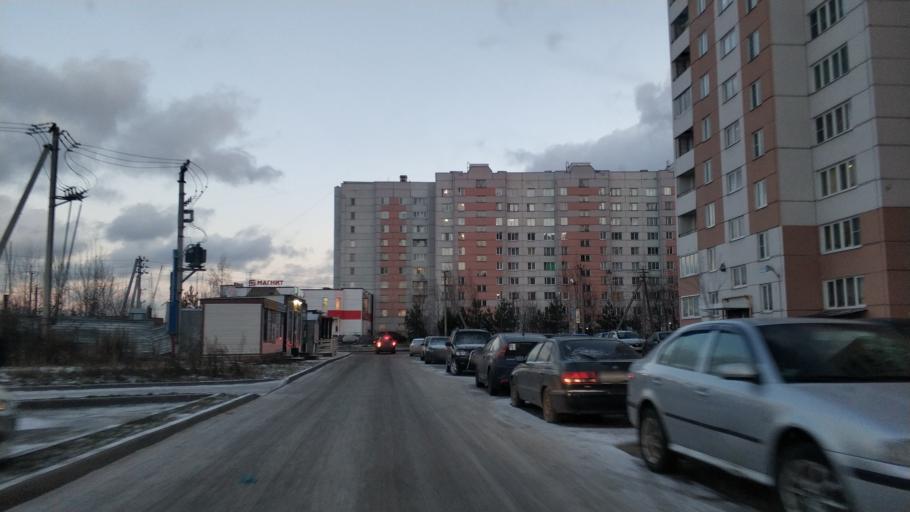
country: RU
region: St.-Petersburg
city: Pontonnyy
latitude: 59.8004
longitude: 30.6365
